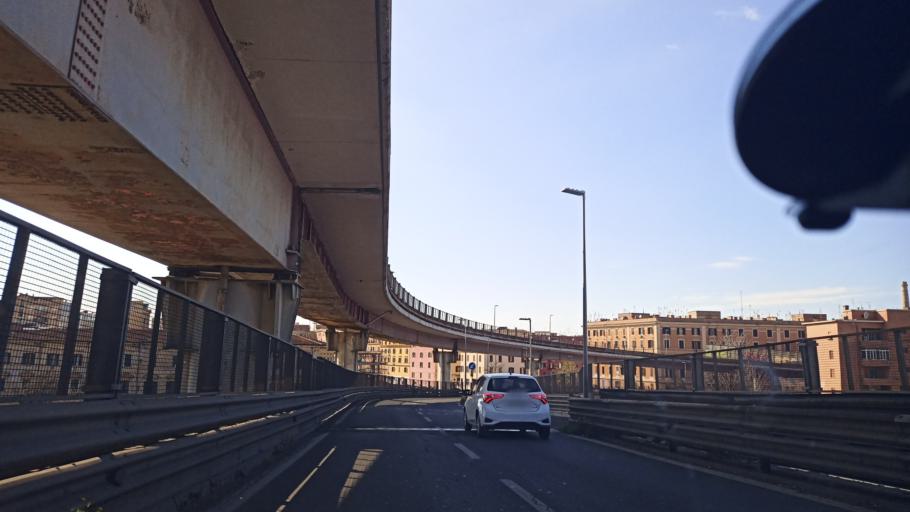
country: IT
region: Latium
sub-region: Citta metropolitana di Roma Capitale
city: Rome
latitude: 41.8935
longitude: 12.5186
